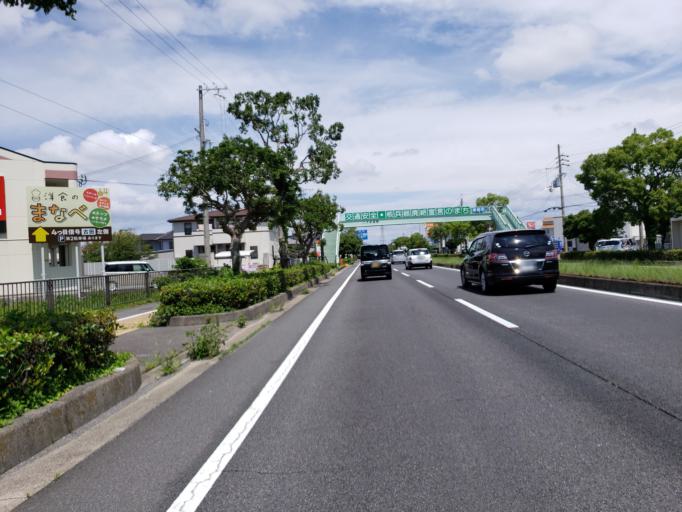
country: JP
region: Hyogo
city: Kakogawacho-honmachi
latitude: 34.7136
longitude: 134.8788
